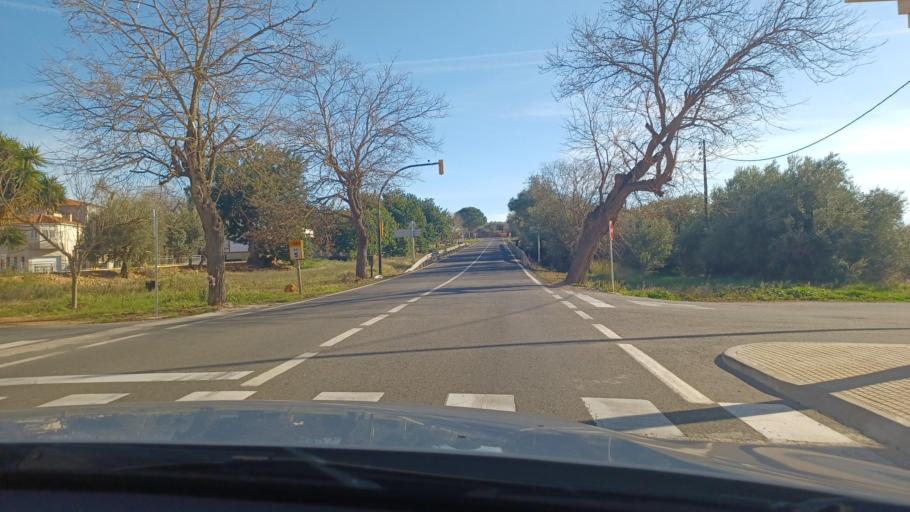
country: ES
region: Catalonia
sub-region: Provincia de Tarragona
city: Masdenverge
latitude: 40.7132
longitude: 0.5326
